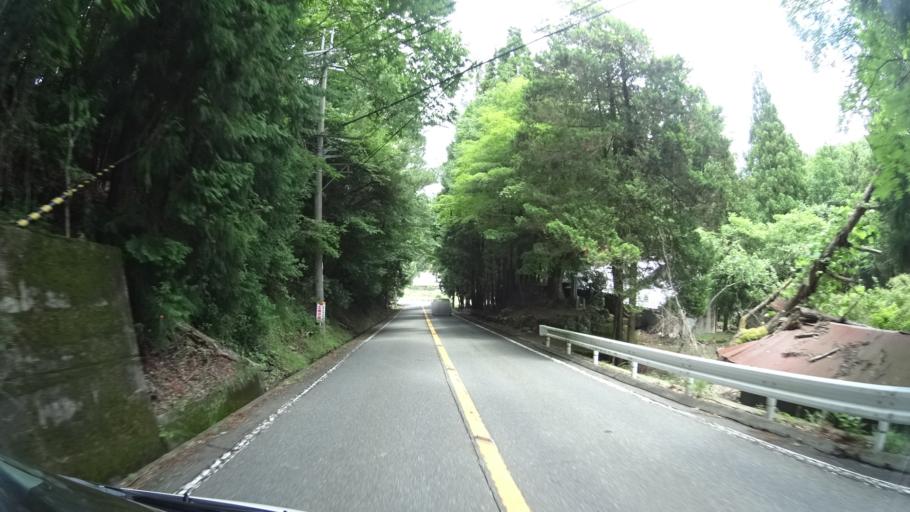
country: JP
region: Kyoto
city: Kameoka
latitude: 35.0398
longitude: 135.4124
